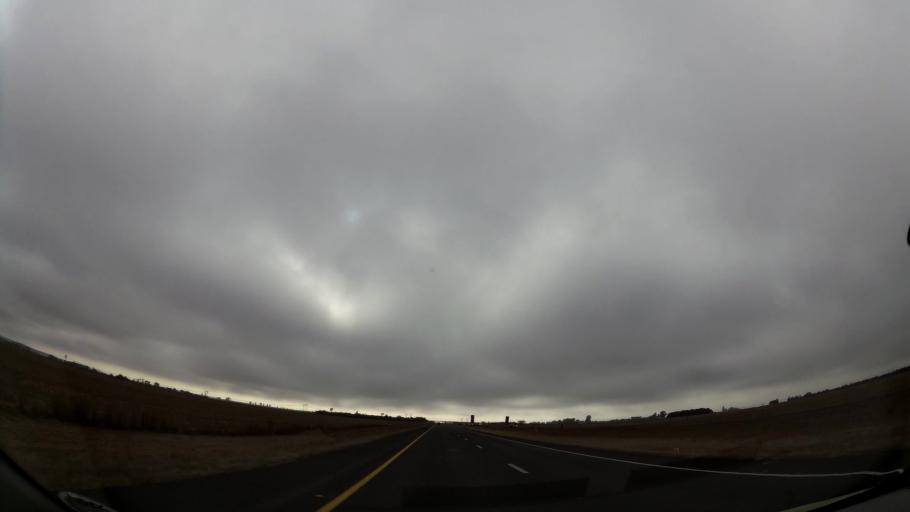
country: ZA
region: Mpumalanga
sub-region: Nkangala District Municipality
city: Delmas
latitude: -26.0621
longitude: 28.7984
